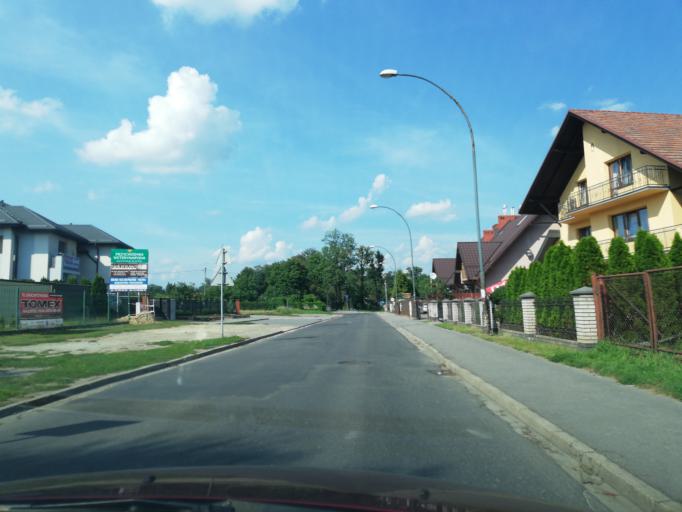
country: PL
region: Lesser Poland Voivodeship
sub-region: Powiat nowosadecki
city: Nowy Sacz
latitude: 49.6140
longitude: 20.6902
